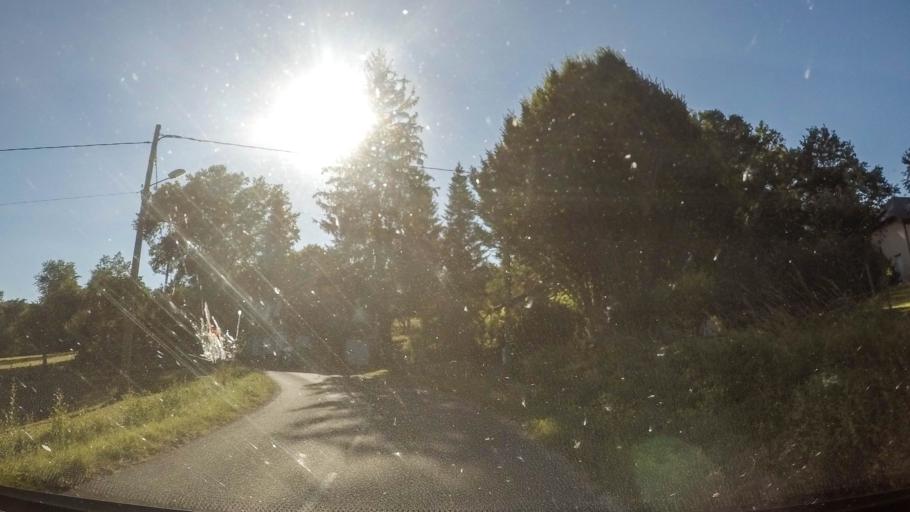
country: FR
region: Midi-Pyrenees
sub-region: Departement de l'Aveyron
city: Saint-Christophe-Vallon
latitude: 44.5505
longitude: 2.4027
